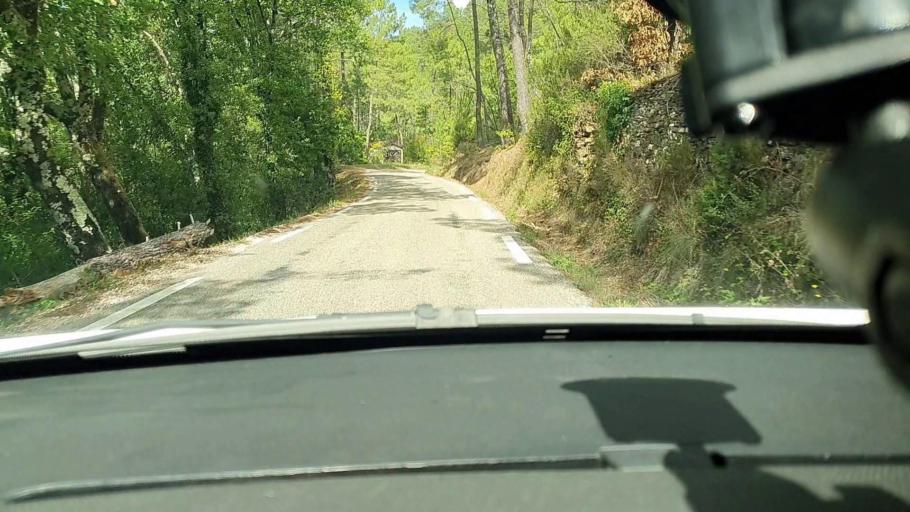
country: FR
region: Languedoc-Roussillon
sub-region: Departement du Gard
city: Besseges
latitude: 44.3084
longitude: 4.0581
